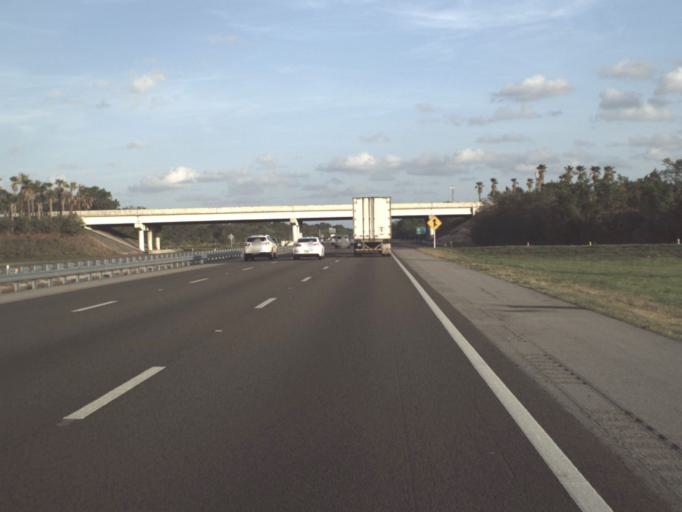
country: US
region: Florida
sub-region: Brevard County
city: Port Saint John
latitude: 28.5029
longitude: -80.8399
